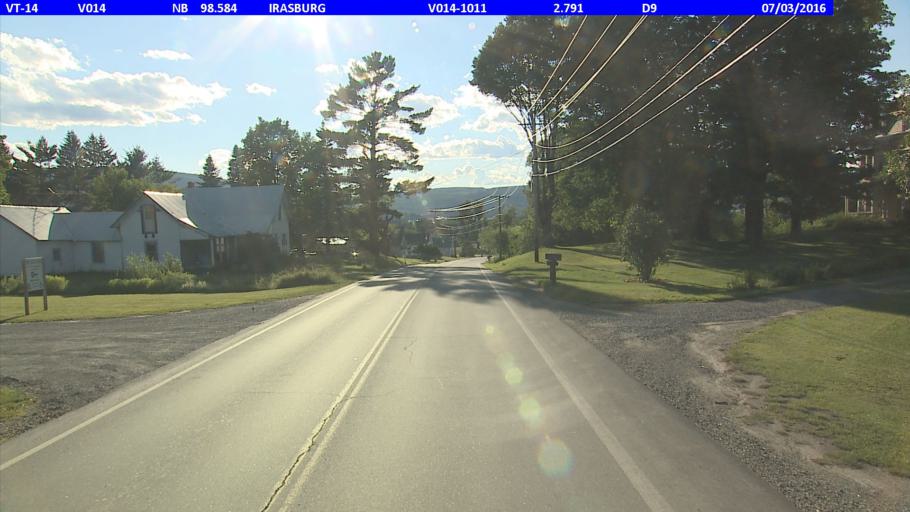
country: US
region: Vermont
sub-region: Orleans County
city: Newport
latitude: 44.8046
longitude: -72.2801
